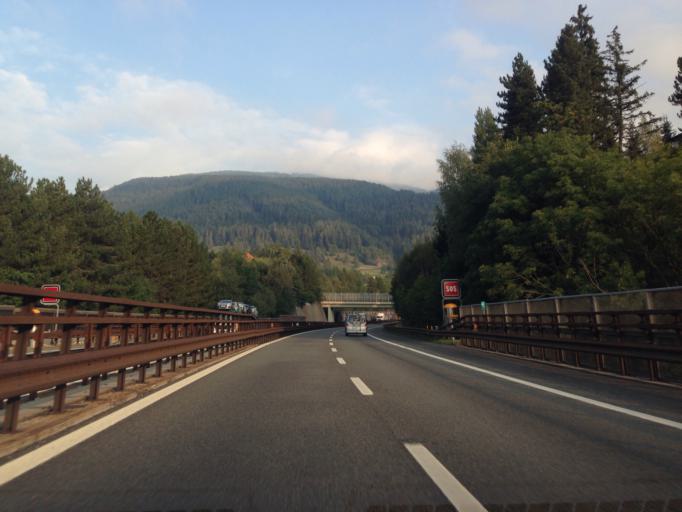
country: IT
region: Trentino-Alto Adige
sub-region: Bolzano
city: Vipiteno
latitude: 46.8874
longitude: 11.4278
